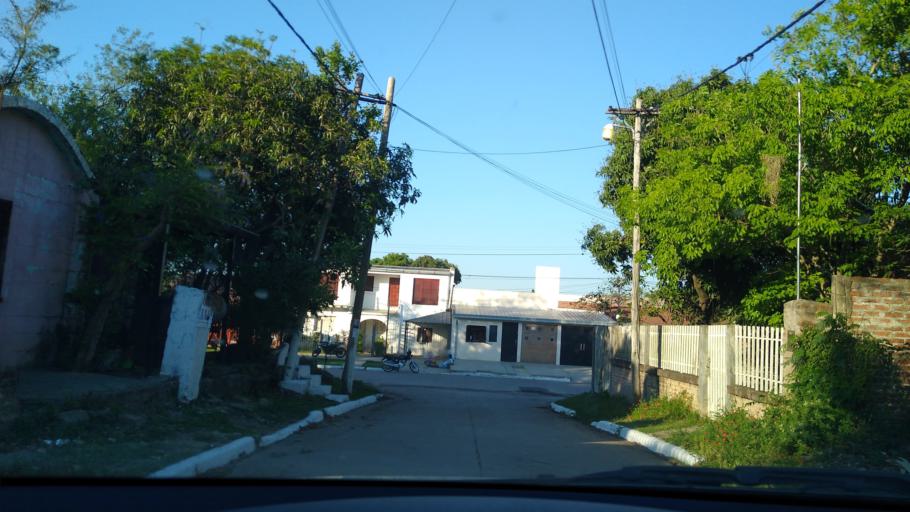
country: AR
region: Chaco
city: Puerto Vilelas
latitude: -27.5113
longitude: -58.9404
